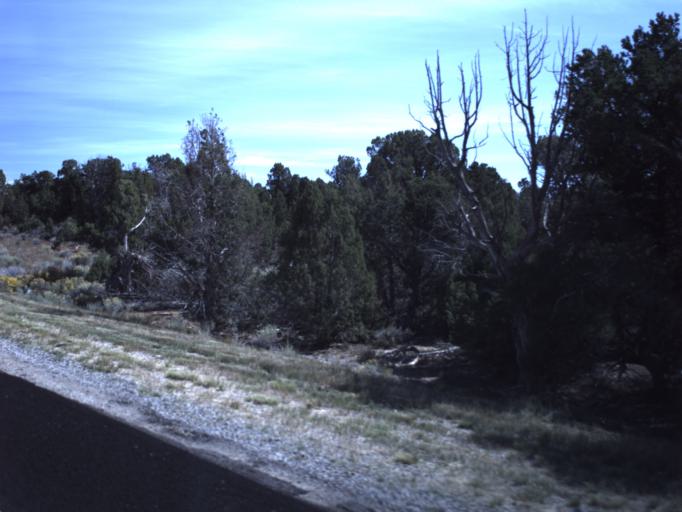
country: US
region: Utah
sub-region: San Juan County
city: Monticello
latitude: 37.8395
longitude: -109.1223
